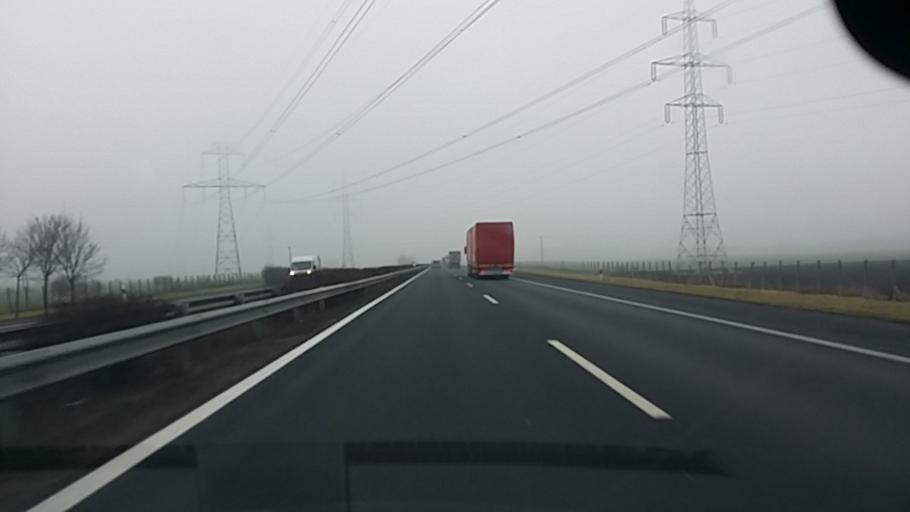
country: HU
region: Gyor-Moson-Sopron
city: Mosonmagyarovar
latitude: 47.8179
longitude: 17.2887
